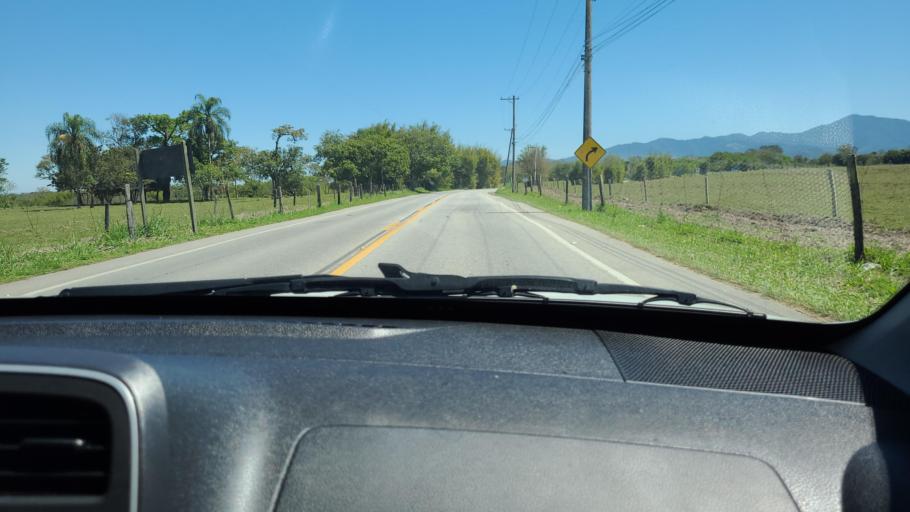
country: BR
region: Sao Paulo
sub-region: Pindamonhangaba
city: Pindamonhangaba
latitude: -22.9013
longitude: -45.4875
